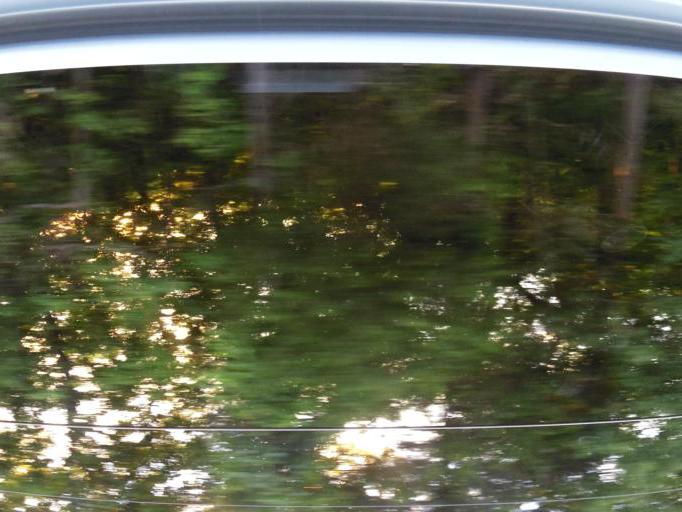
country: US
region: Missouri
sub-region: Jefferson County
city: Cedar Hill
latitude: 38.3251
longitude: -90.6485
